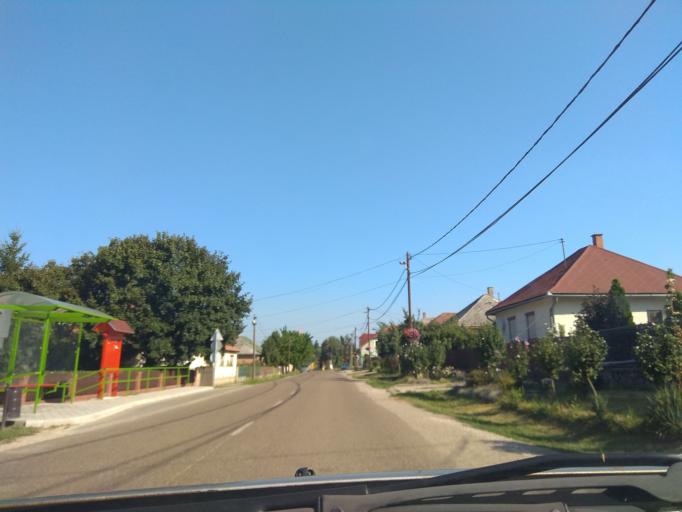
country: HU
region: Borsod-Abauj-Zemplen
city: Emod
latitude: 47.9397
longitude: 20.8162
